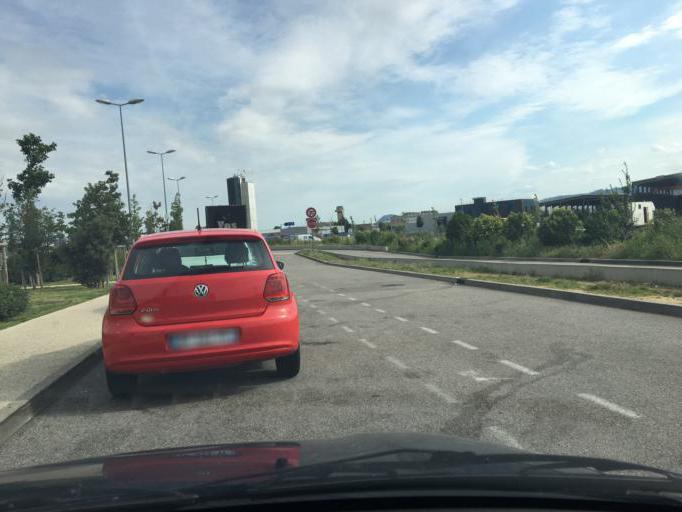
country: FR
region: Rhone-Alpes
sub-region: Departement de la Drome
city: La Roche-de-Glun
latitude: 45.0170
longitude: 4.8742
